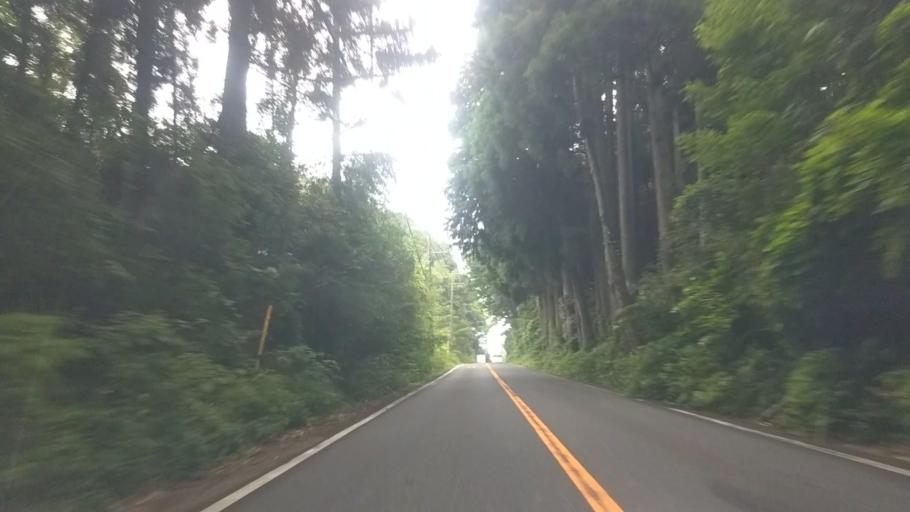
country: JP
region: Chiba
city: Kawaguchi
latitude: 35.2324
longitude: 140.0734
